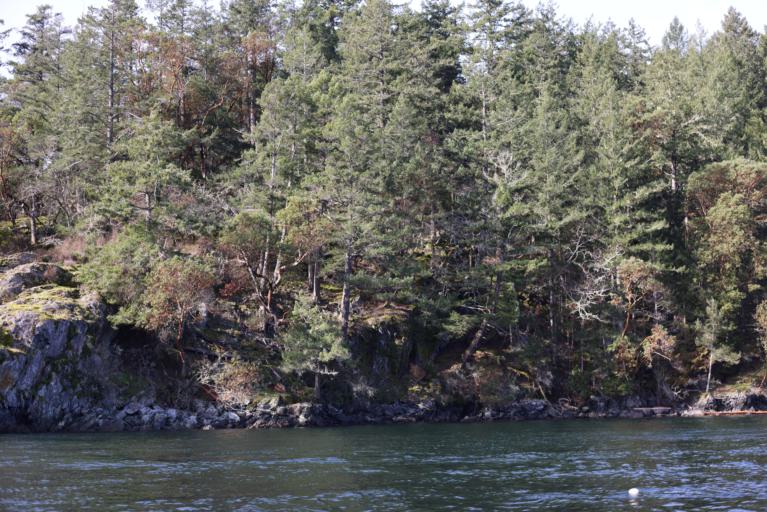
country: CA
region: British Columbia
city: North Cowichan
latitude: 48.7803
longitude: -123.5579
